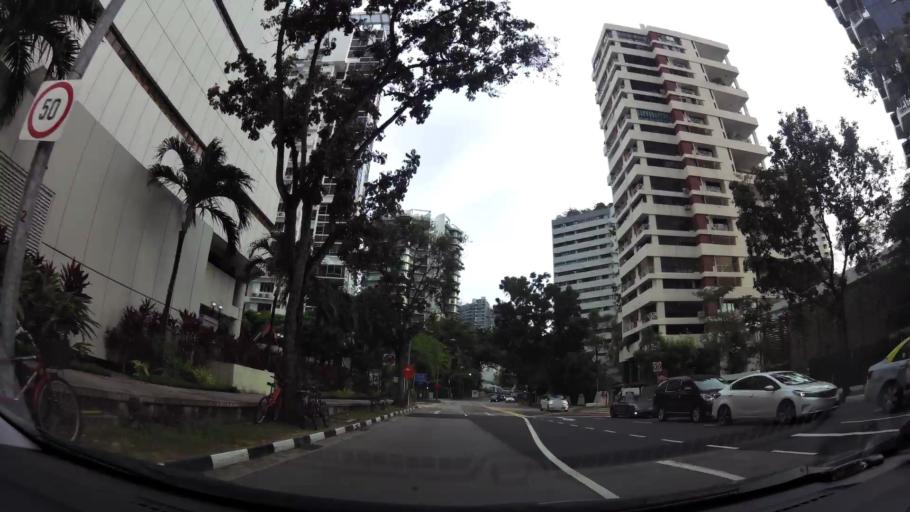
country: SG
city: Singapore
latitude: 1.3102
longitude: 103.8358
